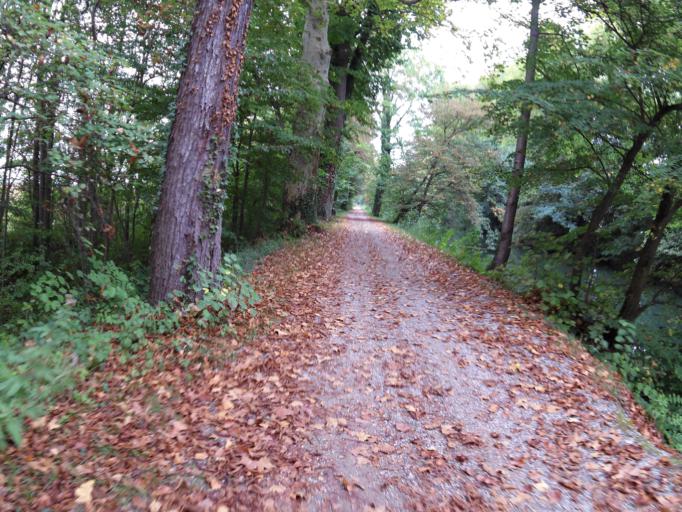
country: FR
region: Alsace
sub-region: Departement du Bas-Rhin
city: Marckolsheim
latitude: 48.1438
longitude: 7.5343
